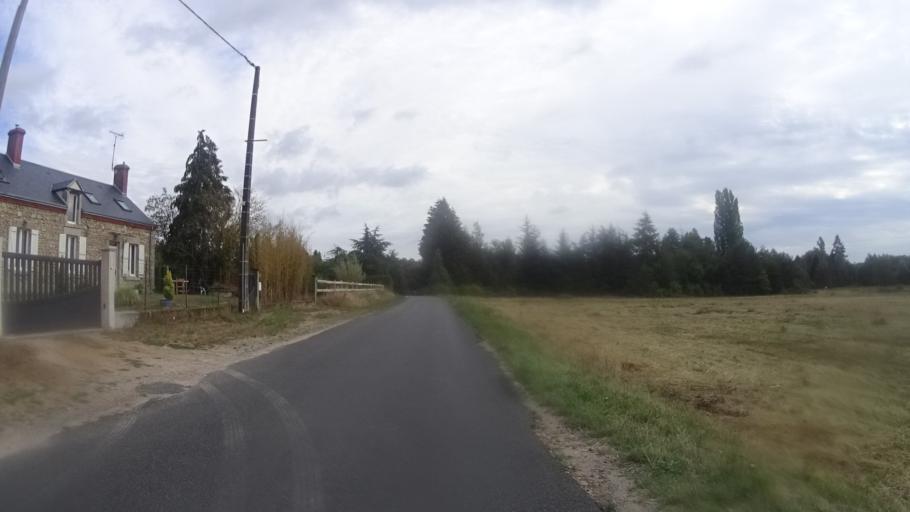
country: FR
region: Centre
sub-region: Departement du Loiret
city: Vitry-aux-Loges
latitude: 47.9963
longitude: 2.2229
